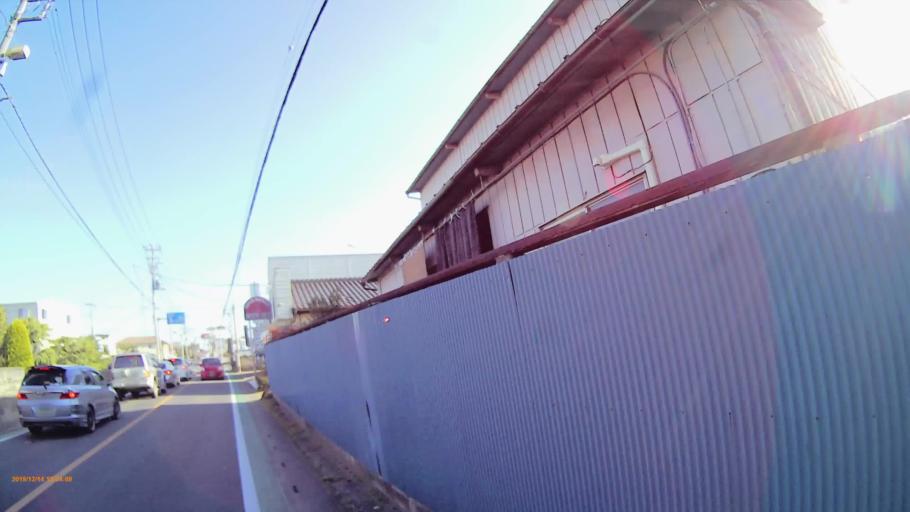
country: JP
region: Saitama
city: Konosu
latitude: 36.0762
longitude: 139.4841
